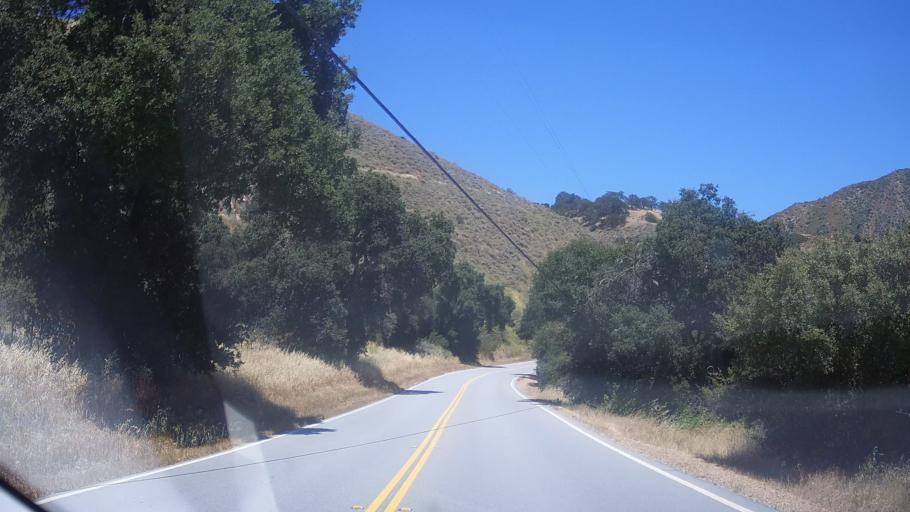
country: US
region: California
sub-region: Monterey County
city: Greenfield
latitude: 36.2424
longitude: -121.4420
